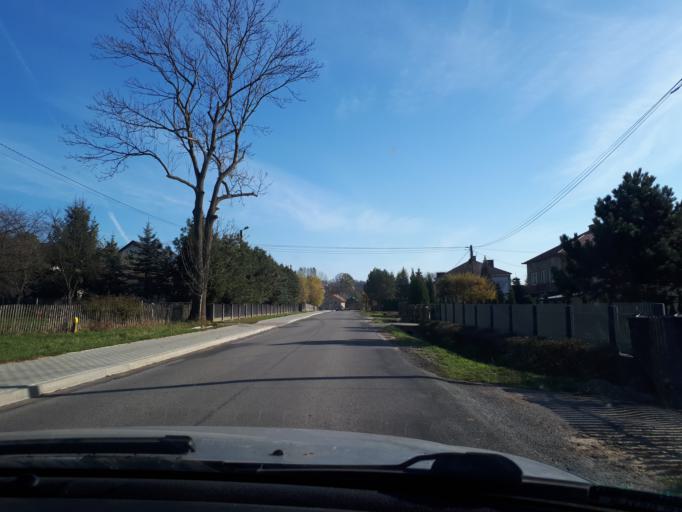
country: PL
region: Subcarpathian Voivodeship
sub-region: Powiat debicki
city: Debica
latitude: 50.0031
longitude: 21.4075
